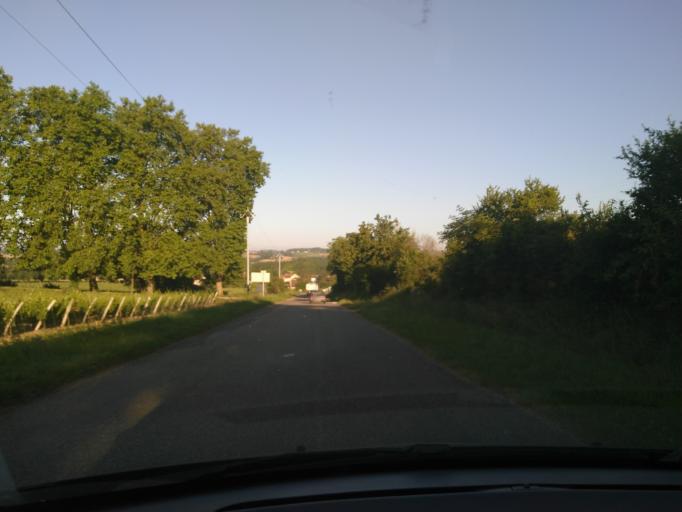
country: FR
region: Midi-Pyrenees
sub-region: Departement du Gers
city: Gondrin
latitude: 43.9037
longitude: 0.3046
